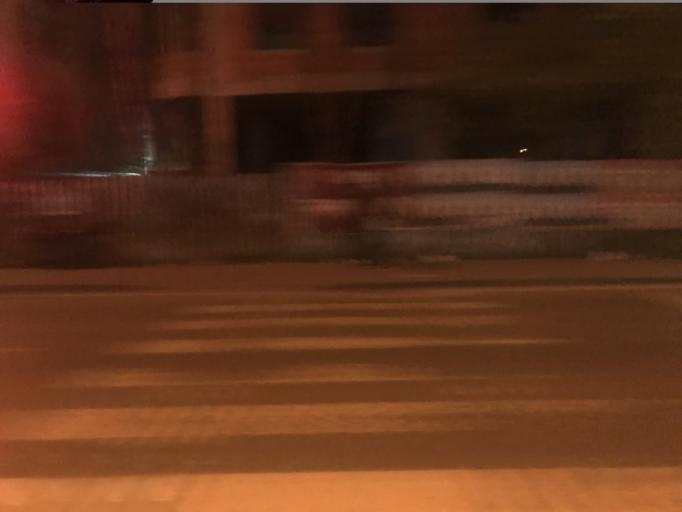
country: TR
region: Istanbul
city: Bahcelievler
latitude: 40.9855
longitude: 28.8722
